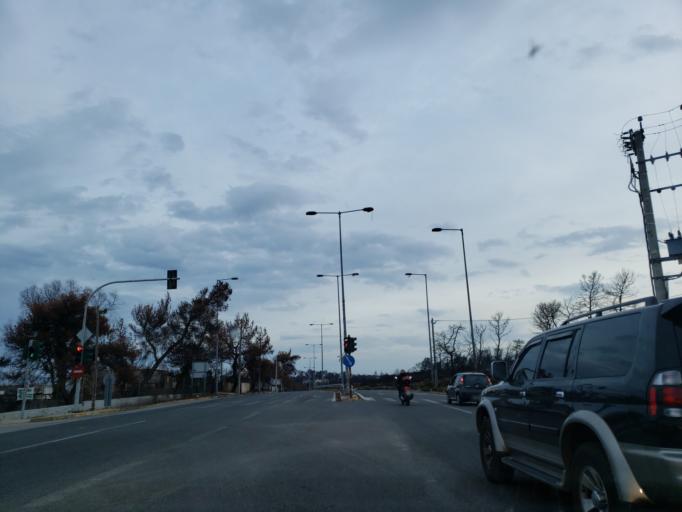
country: GR
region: Attica
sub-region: Nomarchia Anatolikis Attikis
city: Neos Voutzas
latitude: 38.0452
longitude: 23.9885
